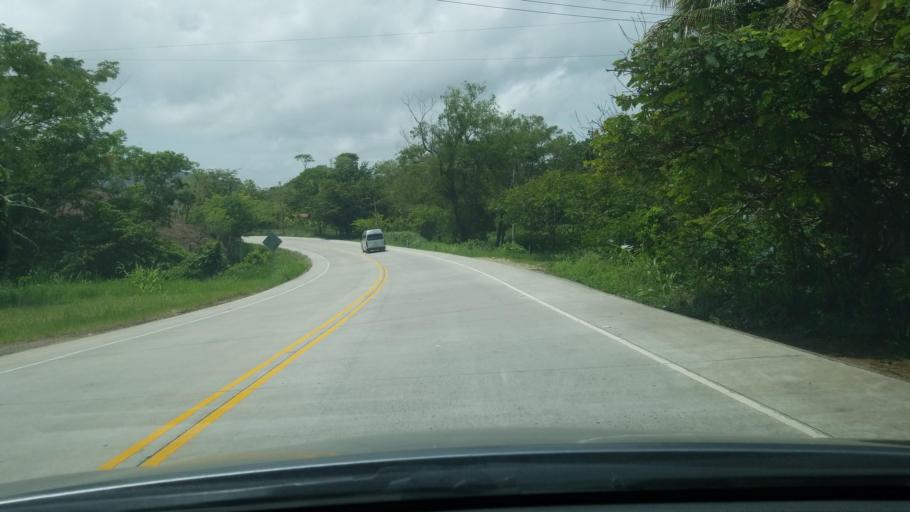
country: HN
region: Copan
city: Trinidad de Copan
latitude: 14.9664
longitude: -88.7788
